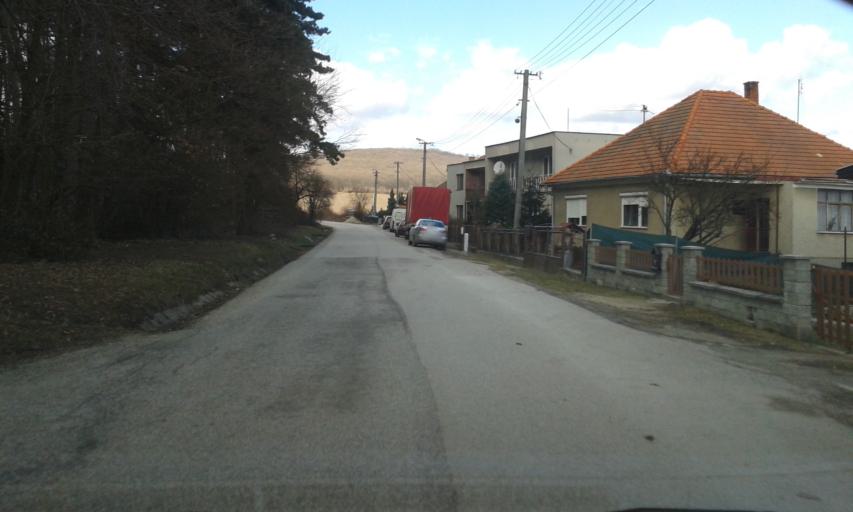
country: SK
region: Nitriansky
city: Zlate Moravce
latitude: 48.4319
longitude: 18.3251
